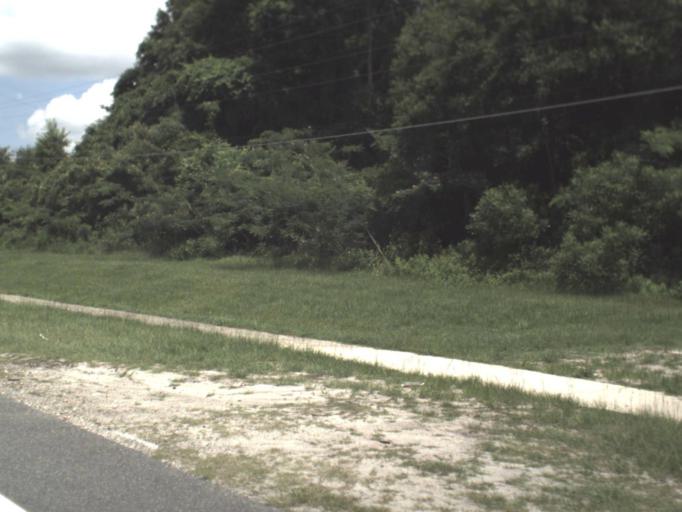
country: US
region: Florida
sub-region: Alachua County
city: High Springs
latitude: 29.8026
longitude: -82.5177
